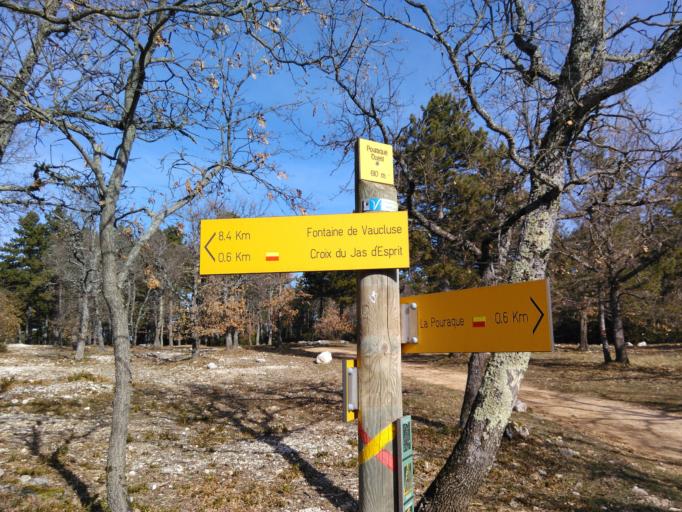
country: FR
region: Provence-Alpes-Cote d'Azur
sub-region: Departement du Vaucluse
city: Venasque
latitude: 43.9559
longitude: 5.1661
